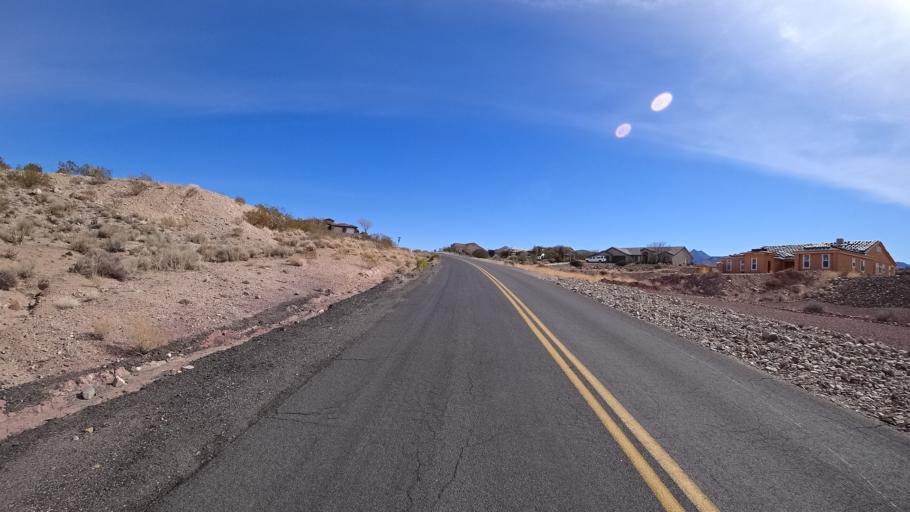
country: US
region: Arizona
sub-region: Mohave County
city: Kingman
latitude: 35.1774
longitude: -114.0036
